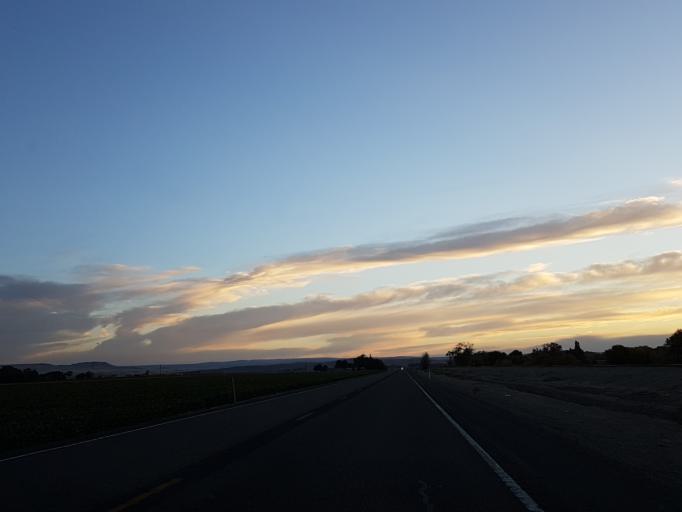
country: US
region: Oregon
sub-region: Malheur County
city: Vale
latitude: 43.9643
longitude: -117.2760
